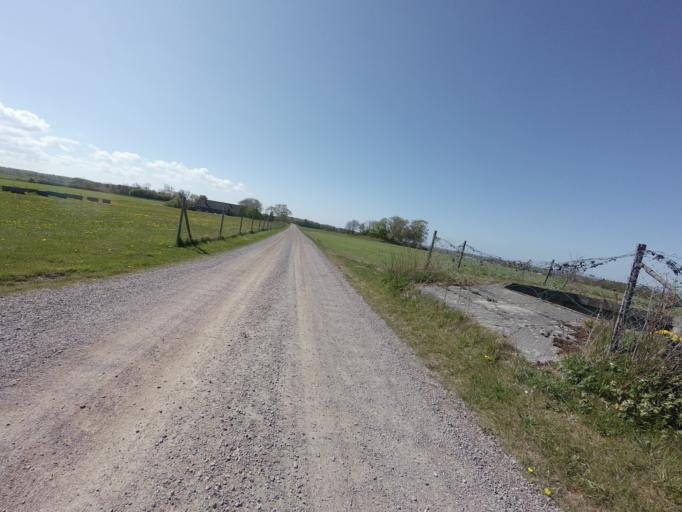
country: DK
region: Capital Region
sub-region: Helsingor Kommune
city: Helsingor
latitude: 56.1298
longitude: 12.6385
